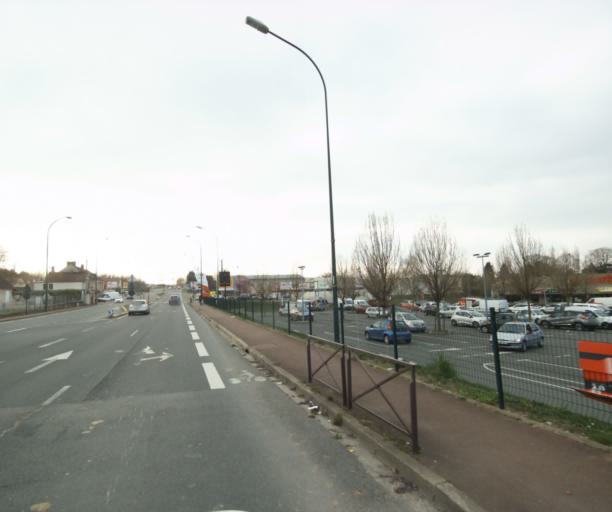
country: FR
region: Ile-de-France
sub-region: Departement du Val-d'Oise
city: Vaureal
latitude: 49.0547
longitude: 2.0200
